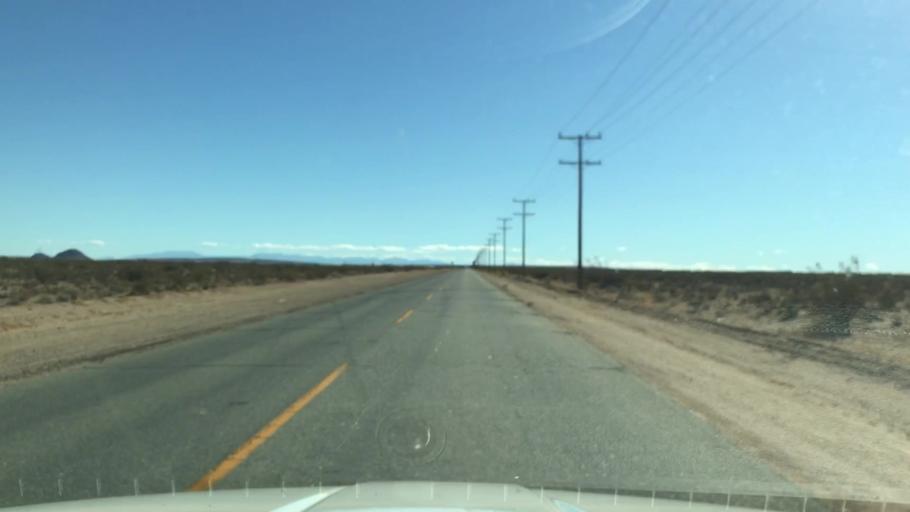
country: US
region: California
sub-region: Kern County
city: California City
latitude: 35.1728
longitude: -117.9858
